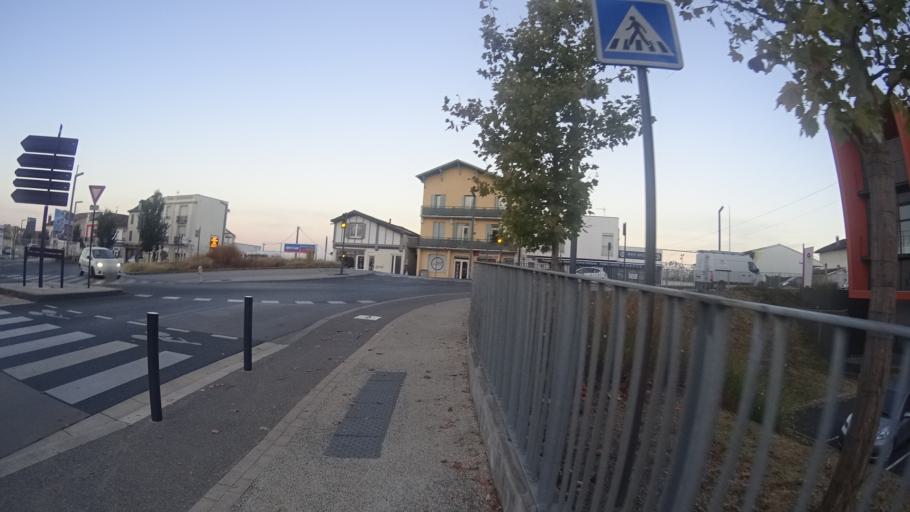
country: FR
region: Aquitaine
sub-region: Departement des Landes
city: Saint-Paul-les-Dax
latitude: 43.7200
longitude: -1.0520
